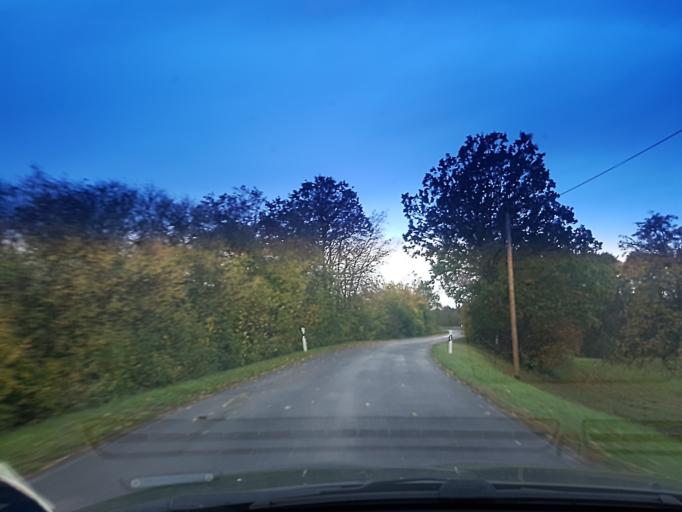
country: DE
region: Bavaria
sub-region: Regierungsbezirk Unterfranken
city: Geiselwind
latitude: 49.7651
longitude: 10.5253
